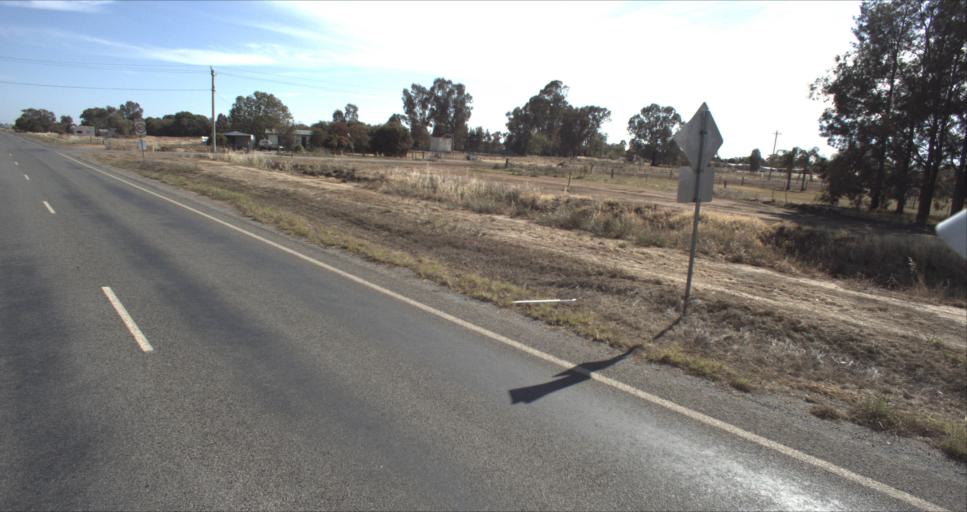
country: AU
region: New South Wales
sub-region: Leeton
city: Leeton
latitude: -34.5964
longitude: 146.4055
